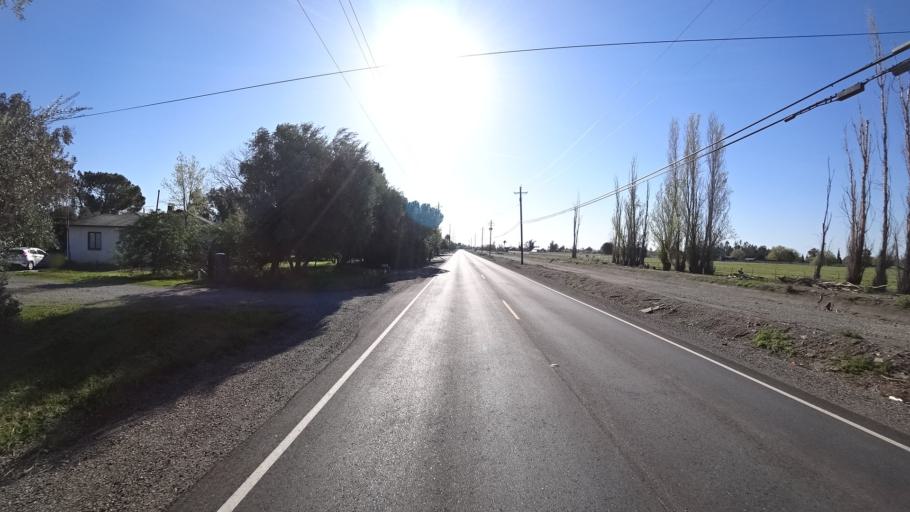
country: US
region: California
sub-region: Glenn County
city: Orland
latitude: 39.7623
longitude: -122.2354
